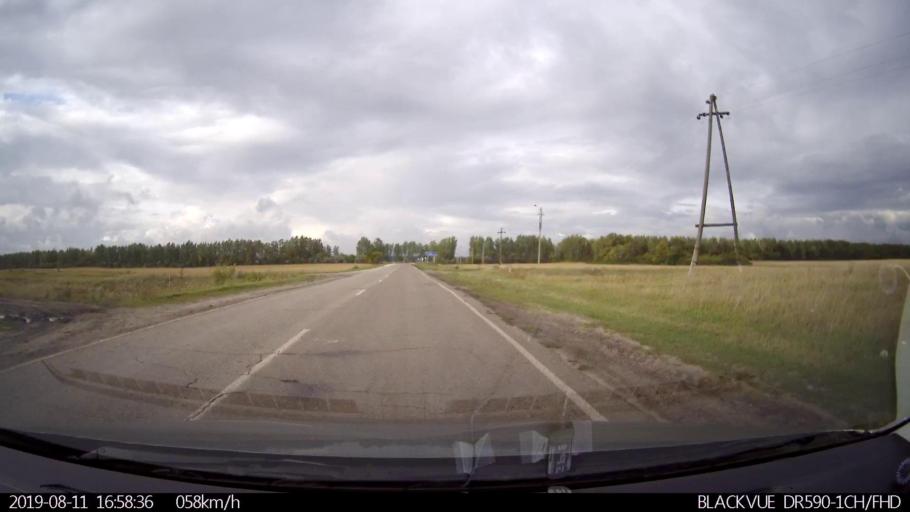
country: RU
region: Ulyanovsk
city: Mayna
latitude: 54.3096
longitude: 47.6565
